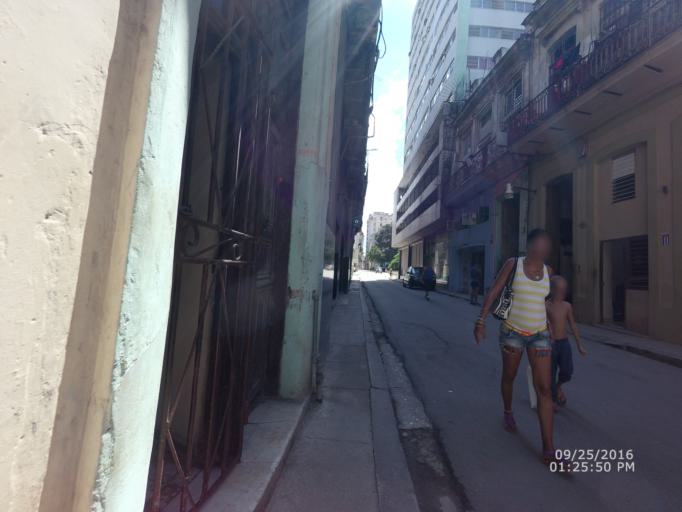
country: CU
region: La Habana
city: Centro Habana
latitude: 23.1410
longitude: -82.3539
